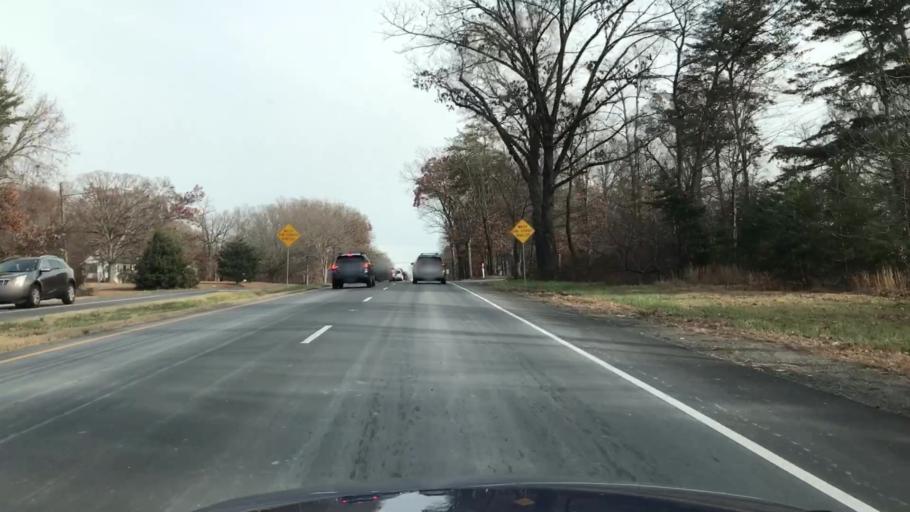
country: US
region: Virginia
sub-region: Fairfax County
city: Mantua
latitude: 38.8652
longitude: -77.2513
